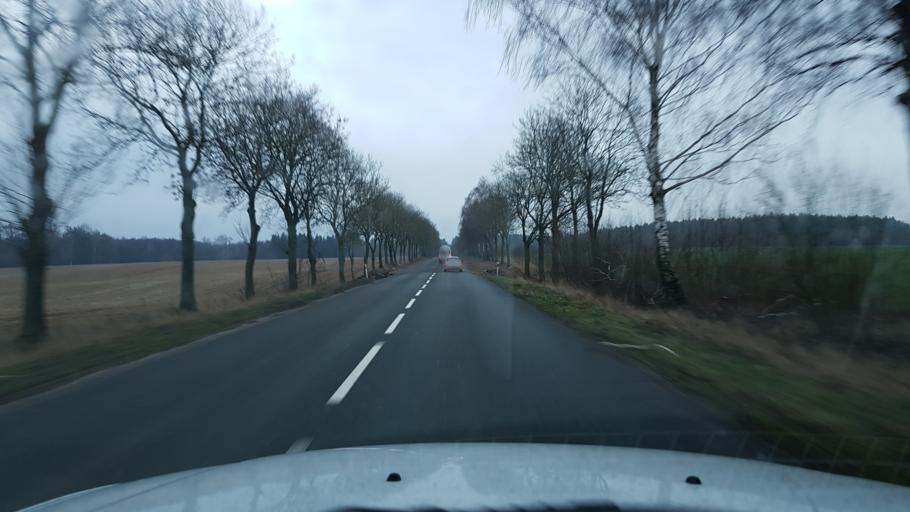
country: PL
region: West Pomeranian Voivodeship
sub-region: Powiat gryficki
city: Gryfice
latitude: 53.8660
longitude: 15.2192
